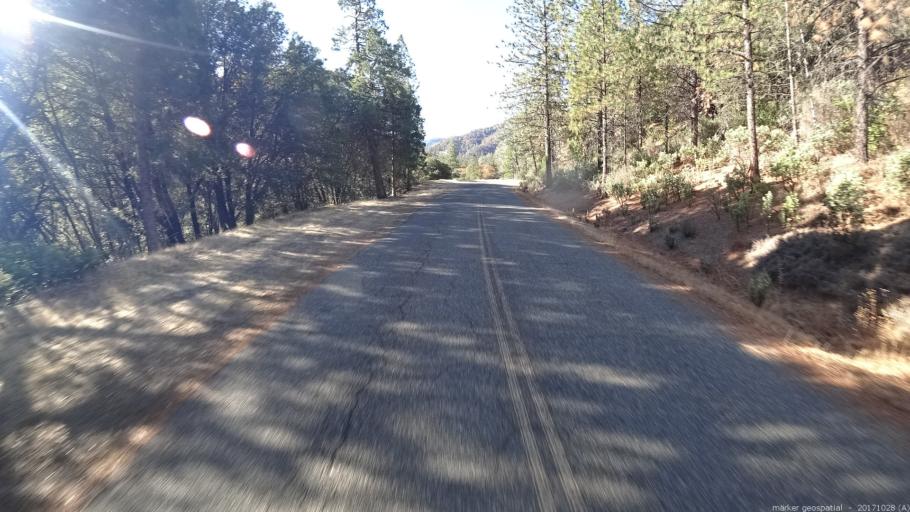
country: US
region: California
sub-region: Trinity County
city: Lewiston
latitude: 40.6600
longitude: -122.6607
